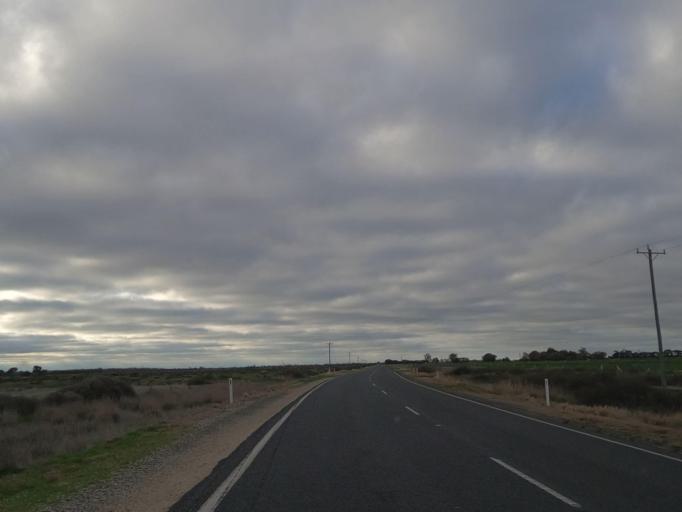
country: AU
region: Victoria
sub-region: Swan Hill
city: Swan Hill
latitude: -35.8424
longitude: 143.9388
